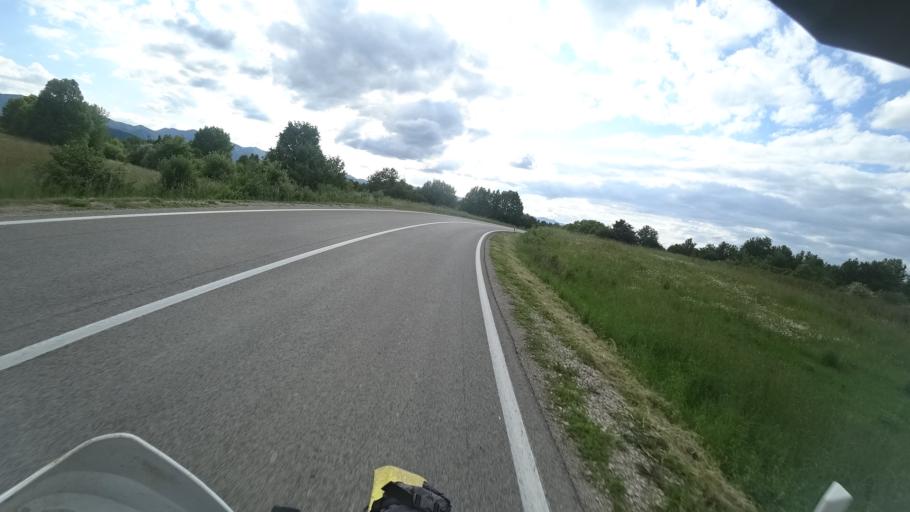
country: HR
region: Licko-Senjska
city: Gospic
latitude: 44.5108
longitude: 15.4290
